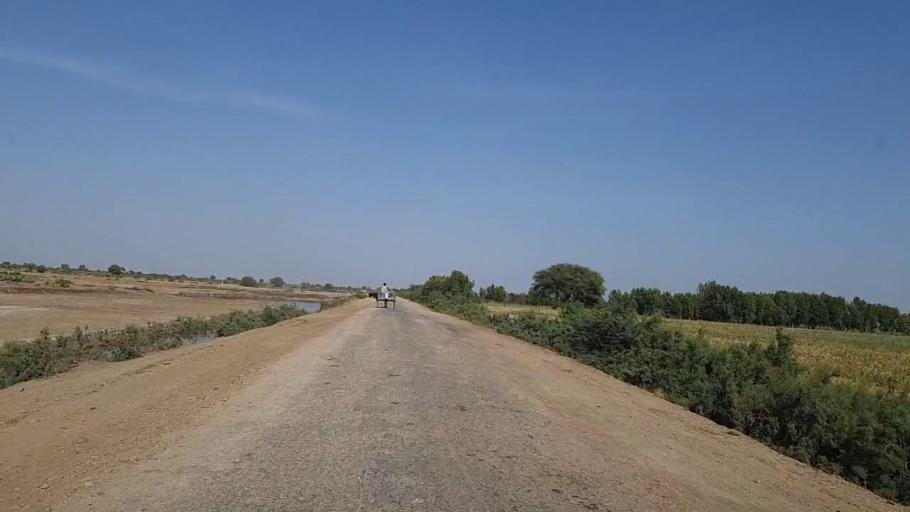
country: PK
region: Sindh
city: Kotri
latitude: 25.1604
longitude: 68.2475
